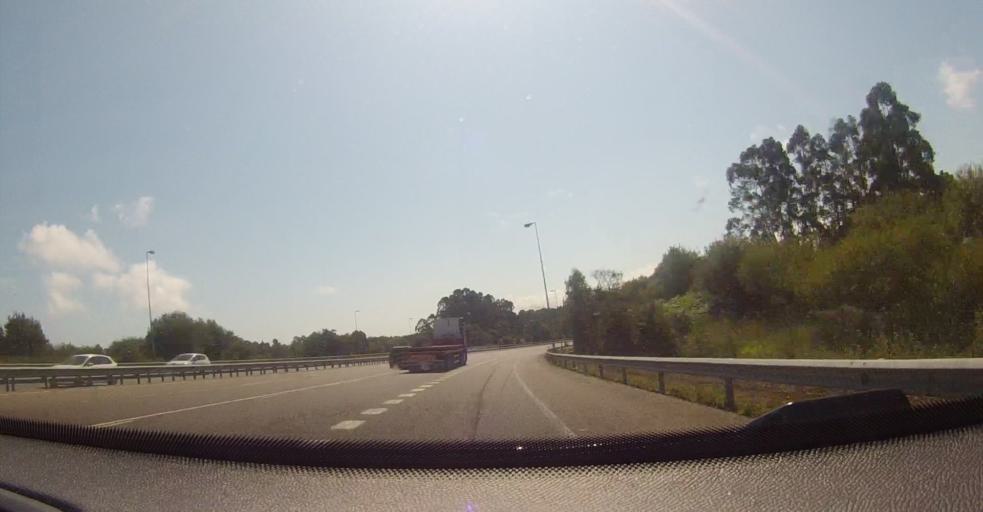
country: ES
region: Asturias
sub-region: Province of Asturias
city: Colunga
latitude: 43.5059
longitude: -5.3355
